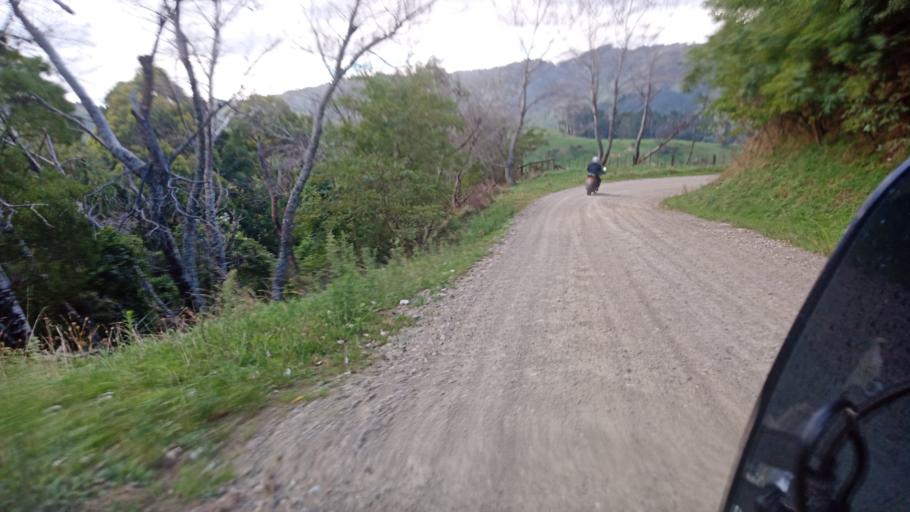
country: NZ
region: Gisborne
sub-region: Gisborne District
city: Gisborne
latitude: -38.4632
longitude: 177.6300
